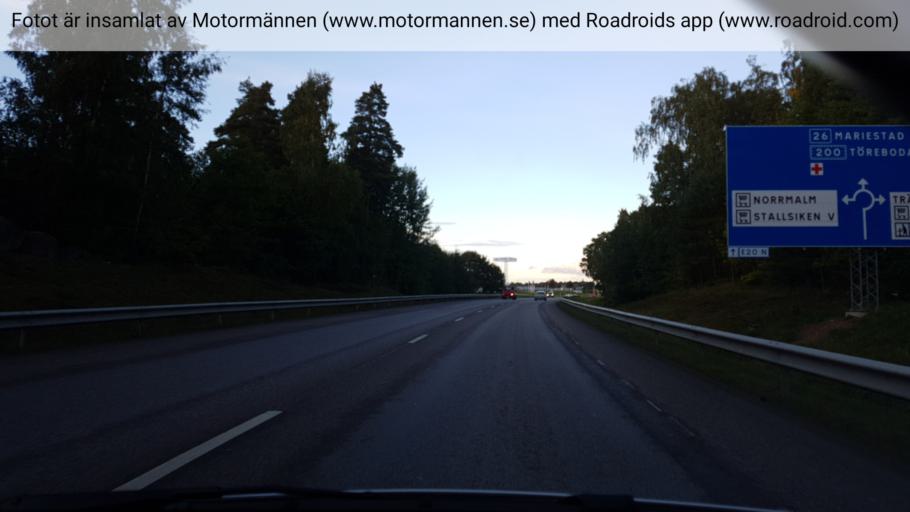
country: SE
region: Vaestra Goetaland
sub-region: Skovde Kommun
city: Skoevde
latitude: 58.4045
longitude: 13.8734
